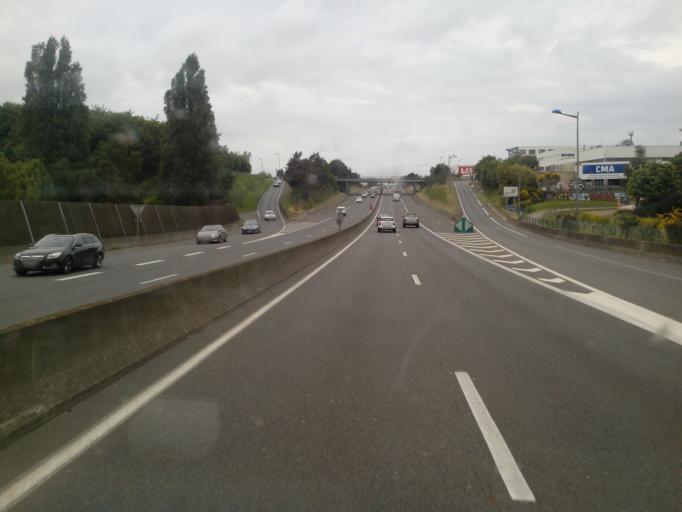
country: FR
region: Brittany
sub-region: Departement des Cotes-d'Armor
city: Langueux
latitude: 48.5037
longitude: -2.7312
